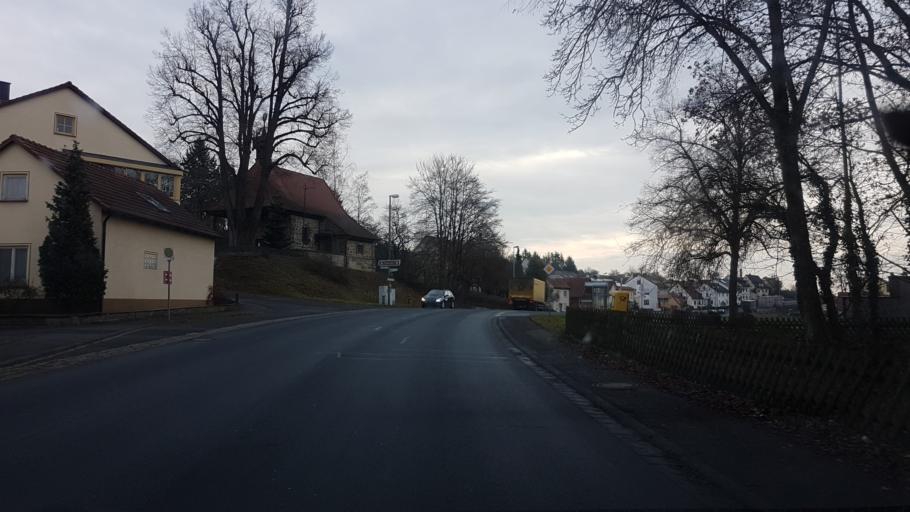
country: DE
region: Bavaria
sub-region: Regierungsbezirk Unterfranken
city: Pfarrweisach
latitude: 50.1708
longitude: 10.7173
